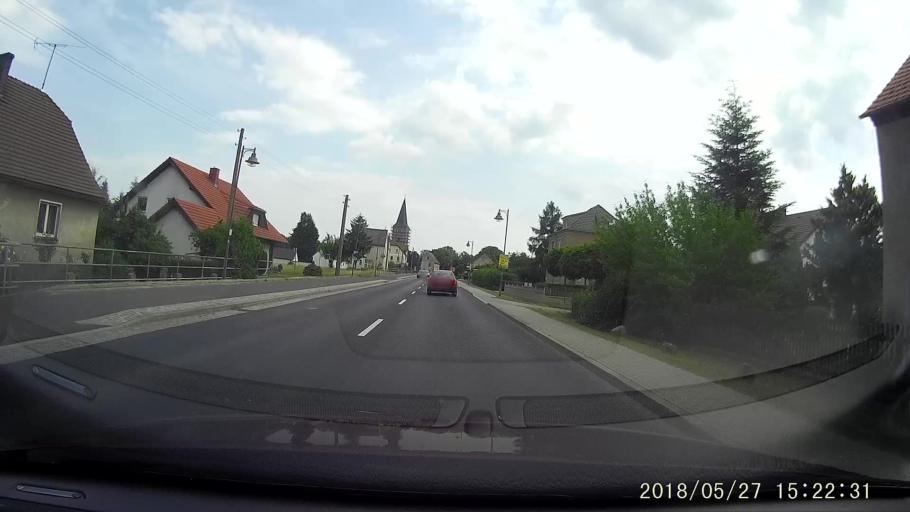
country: DE
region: Saxony
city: Kodersdorf
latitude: 51.2325
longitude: 14.8918
